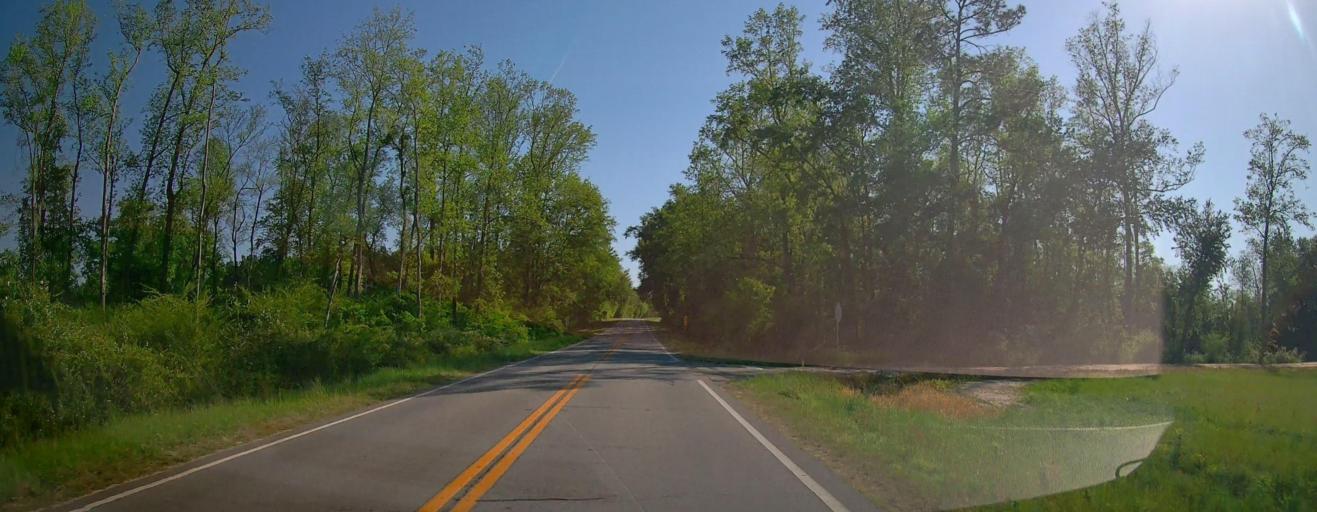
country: US
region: Georgia
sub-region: Wilcox County
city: Rochelle
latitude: 31.9086
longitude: -83.4808
